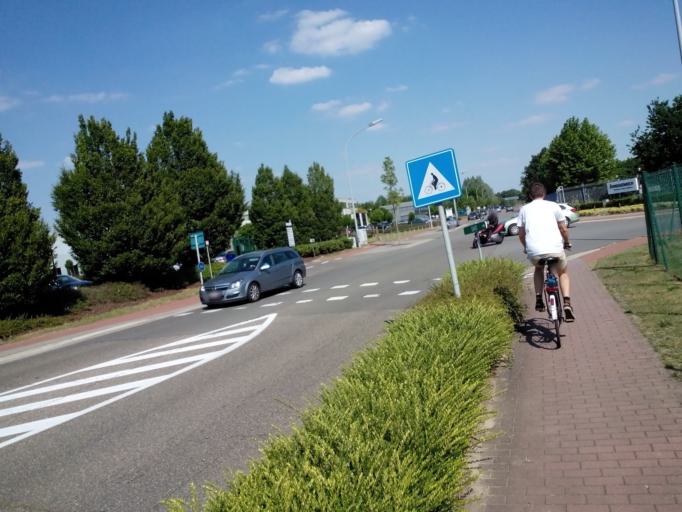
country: BE
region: Flanders
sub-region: Provincie Vlaams-Brabant
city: Leuven
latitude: 50.8534
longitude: 4.7275
